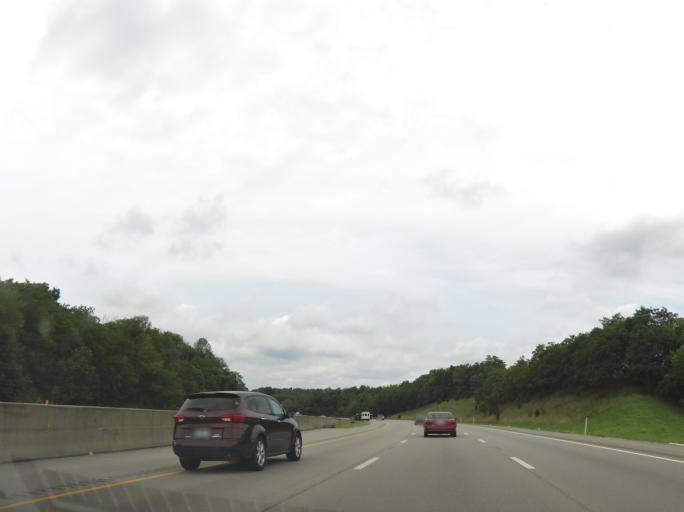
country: US
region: Kentucky
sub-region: Scott County
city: Georgetown
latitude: 38.3192
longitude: -84.5578
